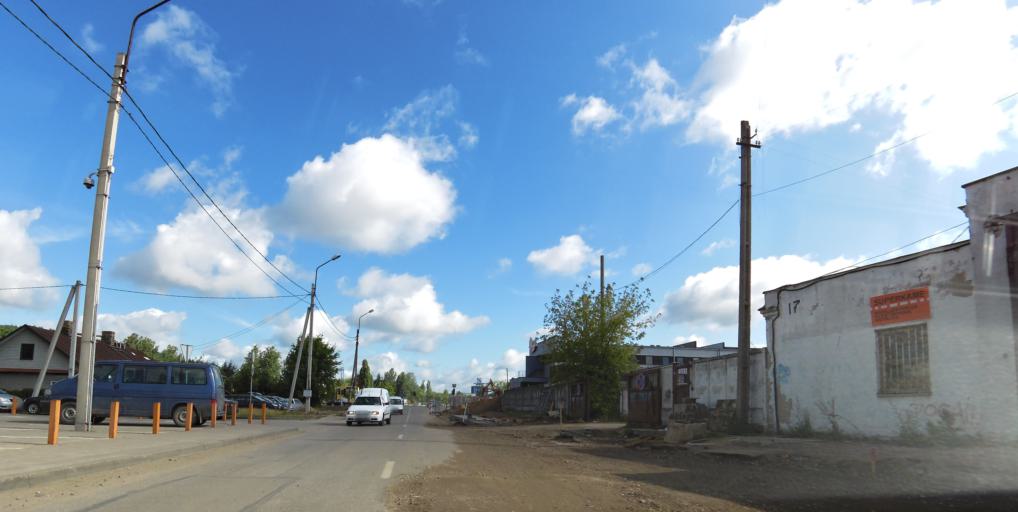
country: LT
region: Vilnius County
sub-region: Vilnius
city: Vilnius
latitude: 54.7037
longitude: 25.2704
